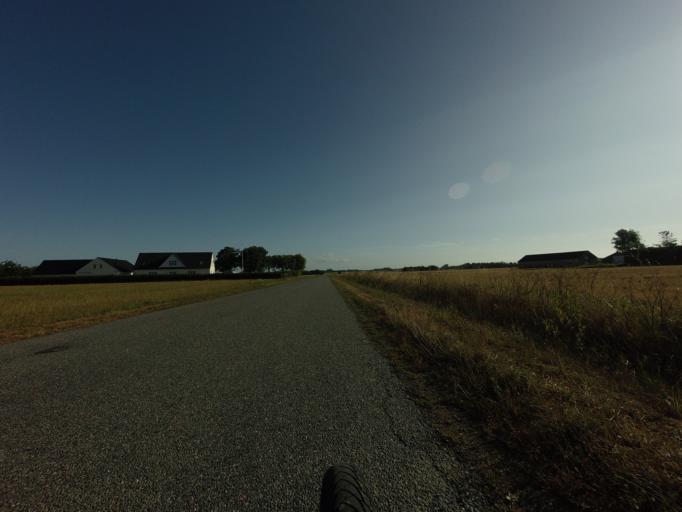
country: DK
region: North Denmark
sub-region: Hjorring Kommune
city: Vra
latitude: 57.3818
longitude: 9.9218
